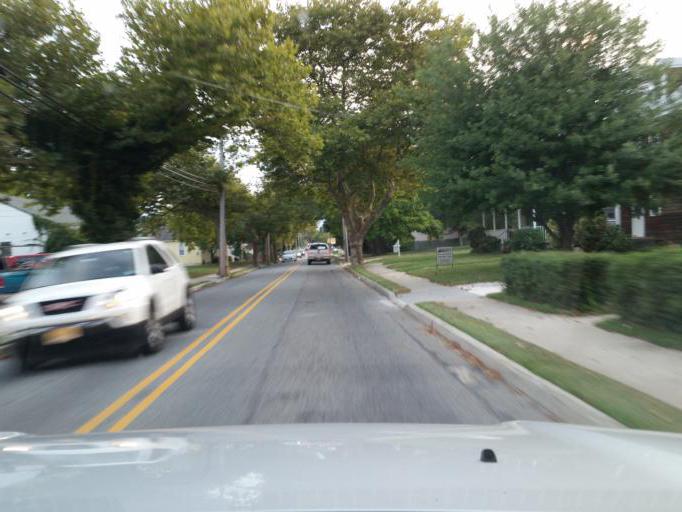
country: US
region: New Jersey
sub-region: Cape May County
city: Cape May
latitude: 38.9450
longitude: -74.9128
